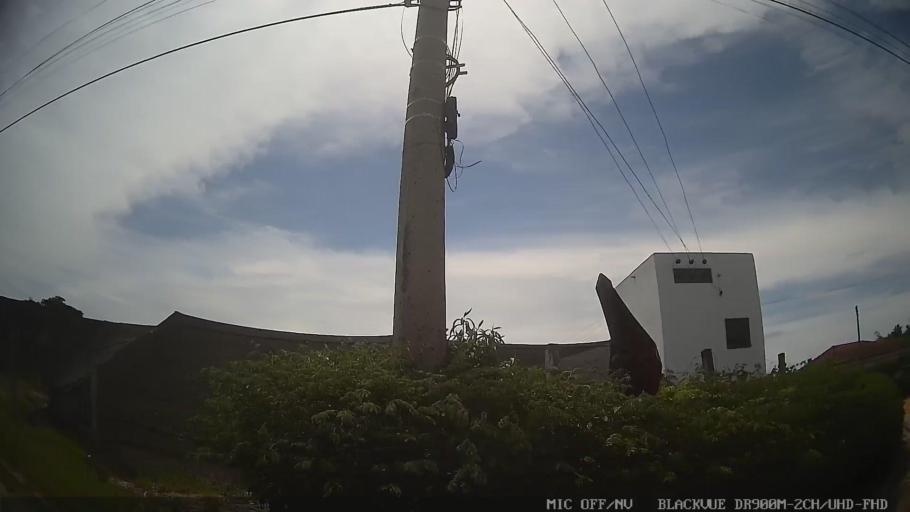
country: BR
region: Sao Paulo
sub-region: Santa Isabel
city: Santa Isabel
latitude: -23.3748
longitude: -46.1790
